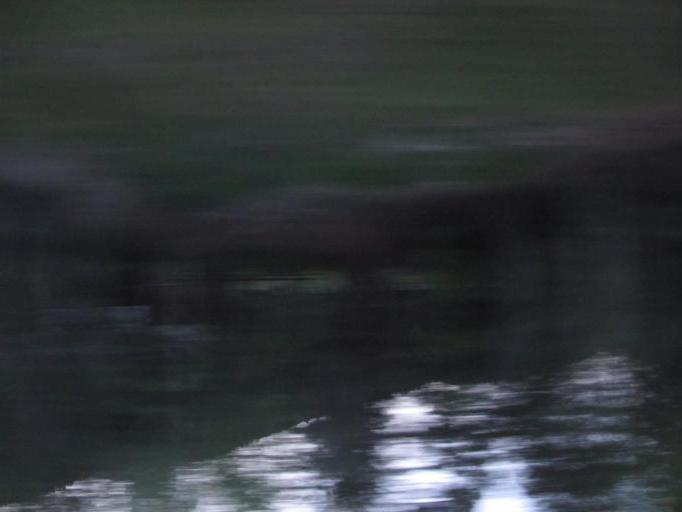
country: NO
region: Oppland
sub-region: Nord-Fron
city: Vinstra
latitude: 61.5846
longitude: 9.8040
